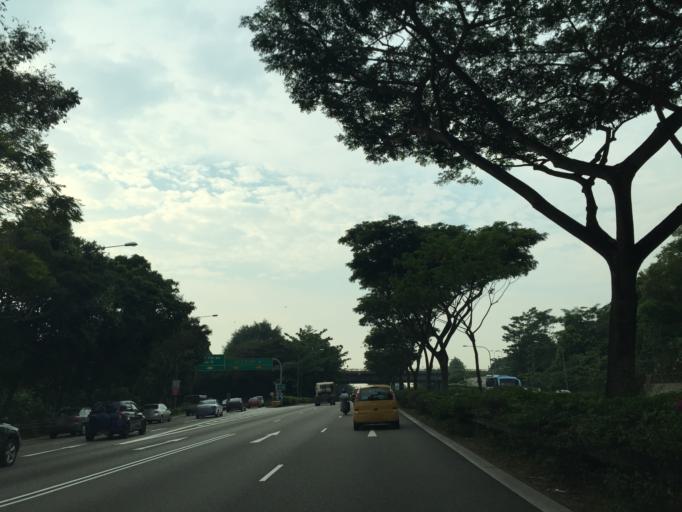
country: MY
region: Johor
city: Johor Bahru
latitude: 1.4175
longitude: 103.7713
